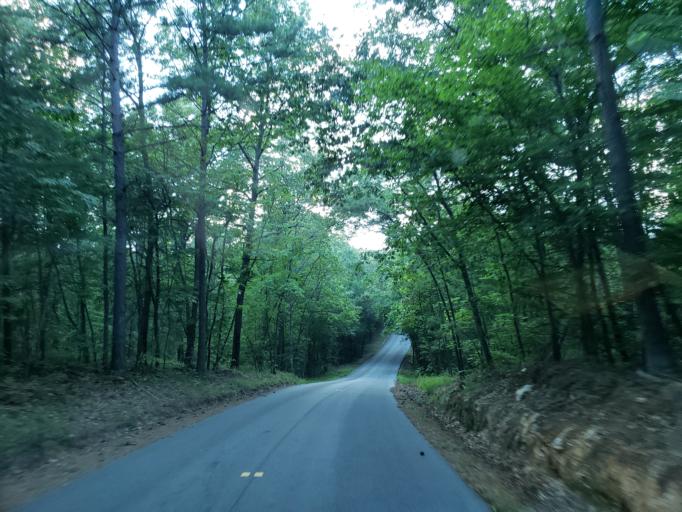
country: US
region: Georgia
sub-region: Paulding County
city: Dallas
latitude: 34.0191
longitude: -84.9030
